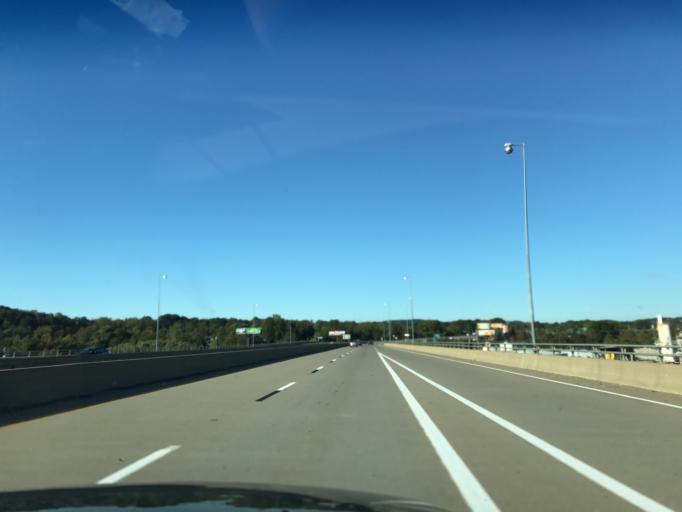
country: US
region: West Virginia
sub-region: Wood County
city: Parkersburg
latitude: 39.2564
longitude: -81.5337
